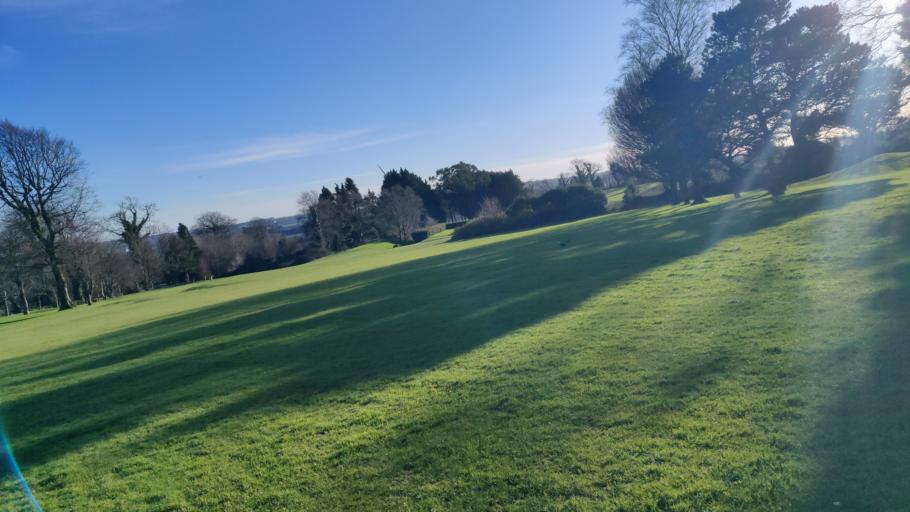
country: IE
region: Munster
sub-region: County Cork
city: Passage West
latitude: 51.8480
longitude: -8.3439
